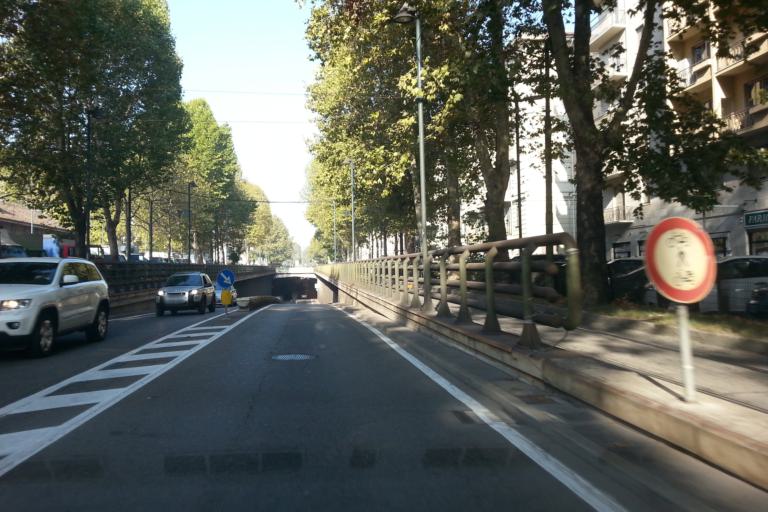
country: IT
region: Piedmont
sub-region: Provincia di Torino
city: Turin
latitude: 45.0751
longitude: 7.6886
